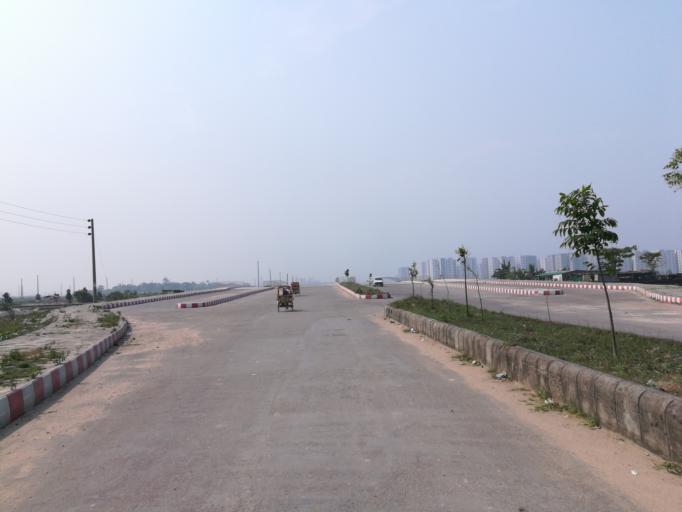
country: BD
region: Dhaka
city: Tungi
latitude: 23.8660
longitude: 90.3607
